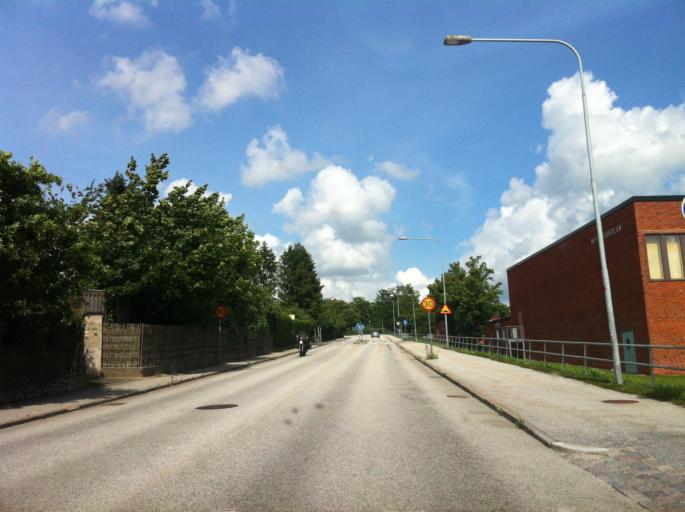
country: SE
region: Skane
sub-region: Skurups Kommun
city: Skurup
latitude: 55.5146
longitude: 13.4232
